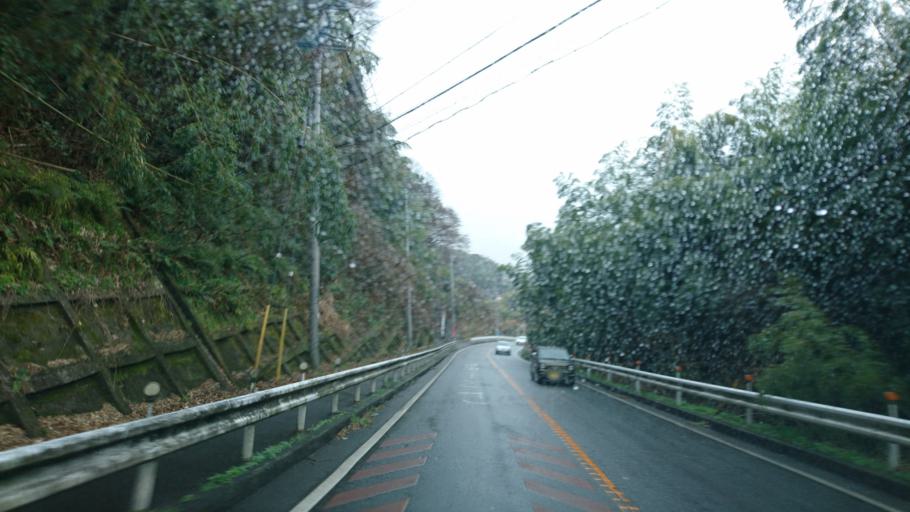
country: JP
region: Kanagawa
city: Zama
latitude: 35.5358
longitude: 139.3297
